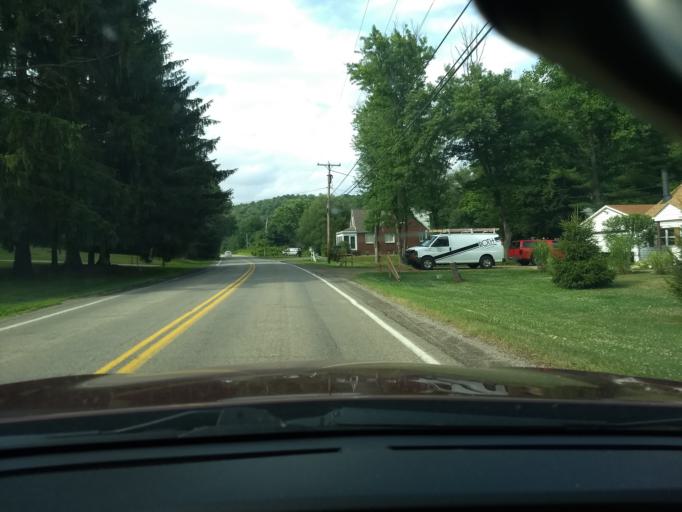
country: US
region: Pennsylvania
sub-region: Allegheny County
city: Bell Acres
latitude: 40.6194
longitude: -80.1404
